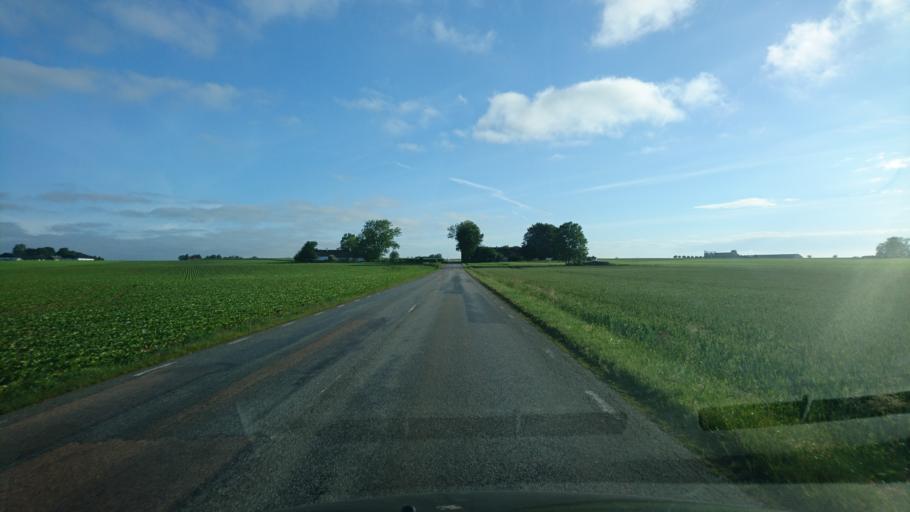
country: SE
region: Skane
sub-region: Tomelilla Kommun
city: Tomelilla
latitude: 55.4767
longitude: 14.0996
